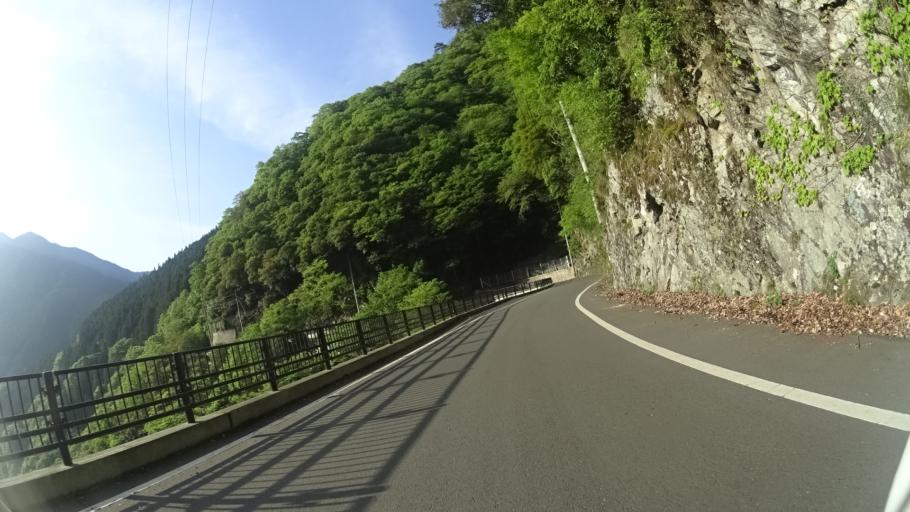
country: JP
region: Tokushima
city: Ikedacho
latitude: 33.9092
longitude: 133.8188
